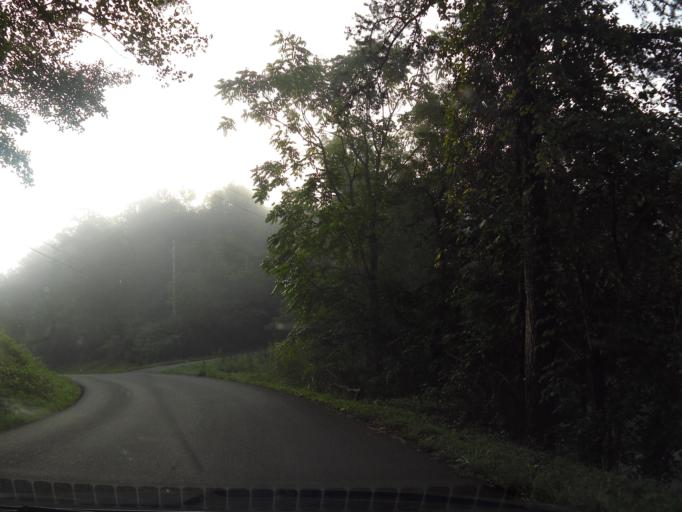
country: US
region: Tennessee
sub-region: Campbell County
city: Jellico
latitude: 36.5776
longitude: -84.1246
